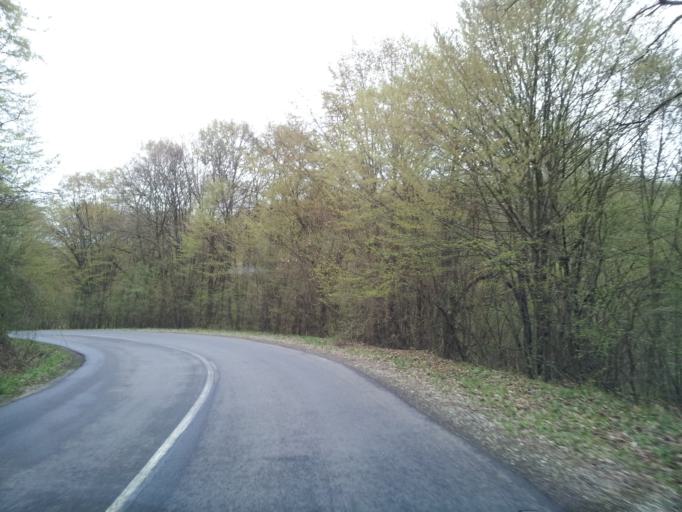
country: HU
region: Borsod-Abauj-Zemplen
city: Rudabanya
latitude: 48.4747
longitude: 20.5412
